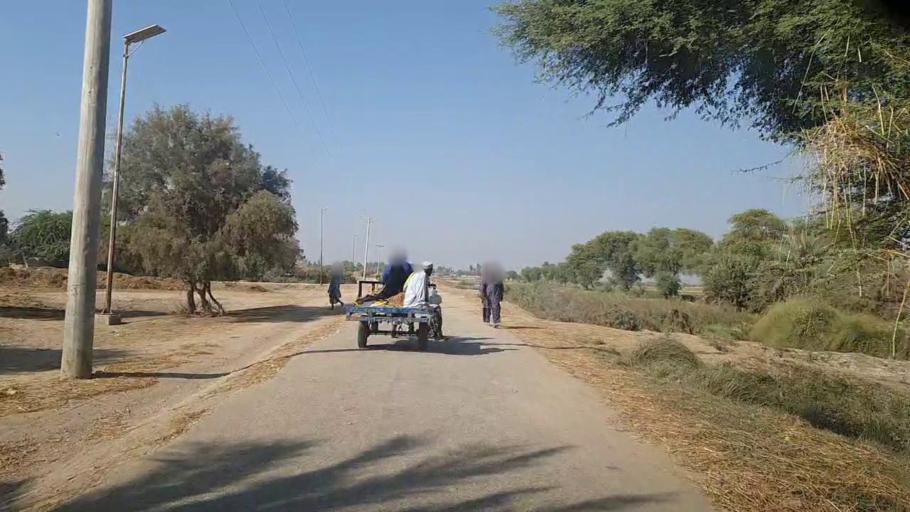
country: PK
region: Sindh
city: Tangwani
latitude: 28.2475
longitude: 68.9961
